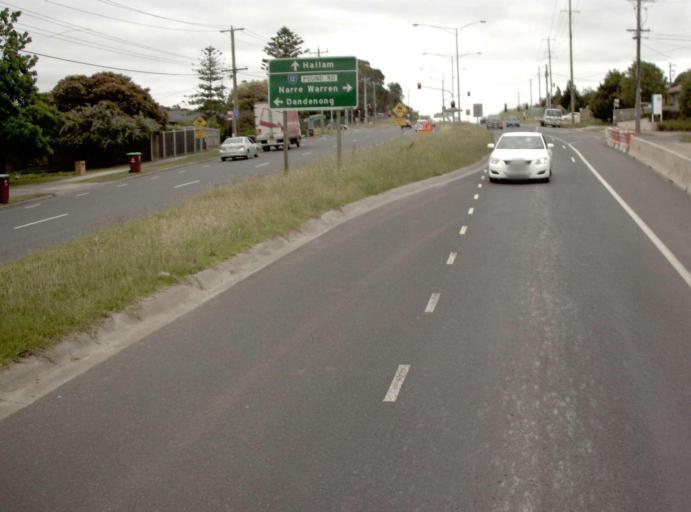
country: AU
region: Victoria
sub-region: Casey
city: Hallam
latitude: -38.0299
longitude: 145.2684
